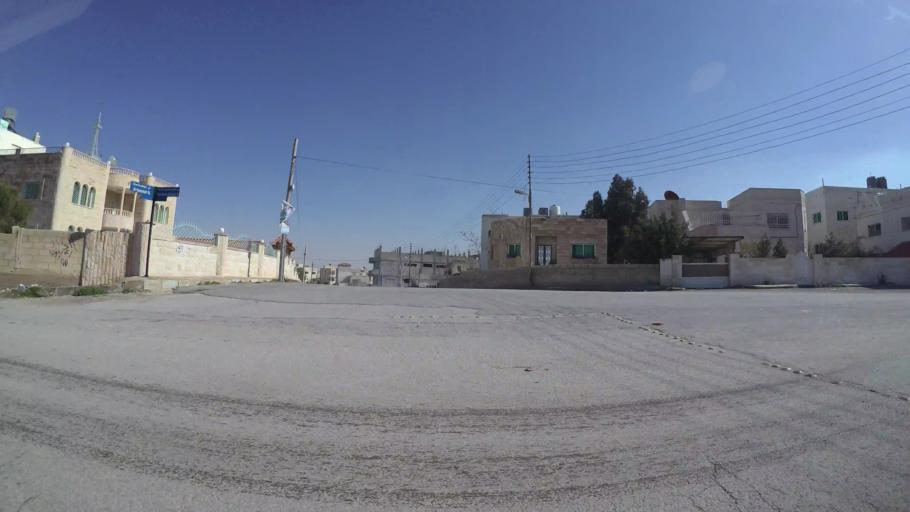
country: JO
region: Zarqa
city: Russeifa
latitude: 32.0400
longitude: 36.0341
